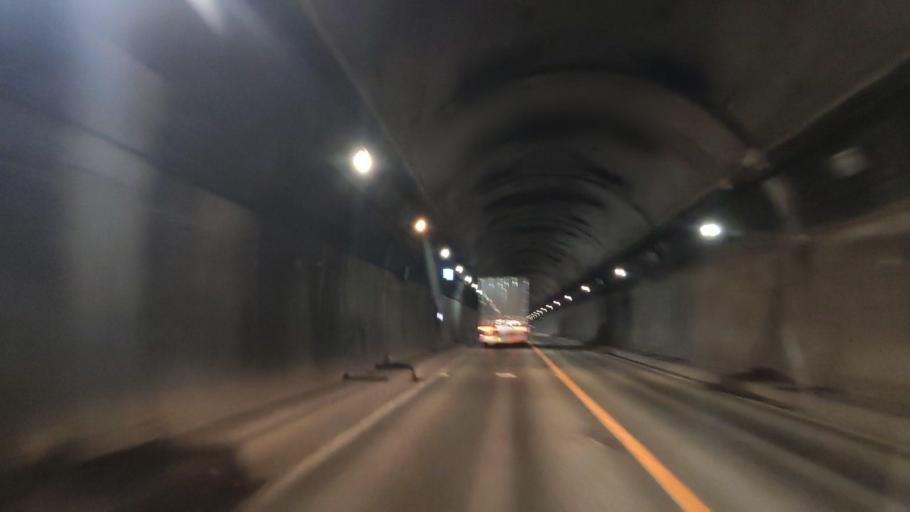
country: JP
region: Aomori
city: Aomori Shi
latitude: 40.7761
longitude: 140.9684
